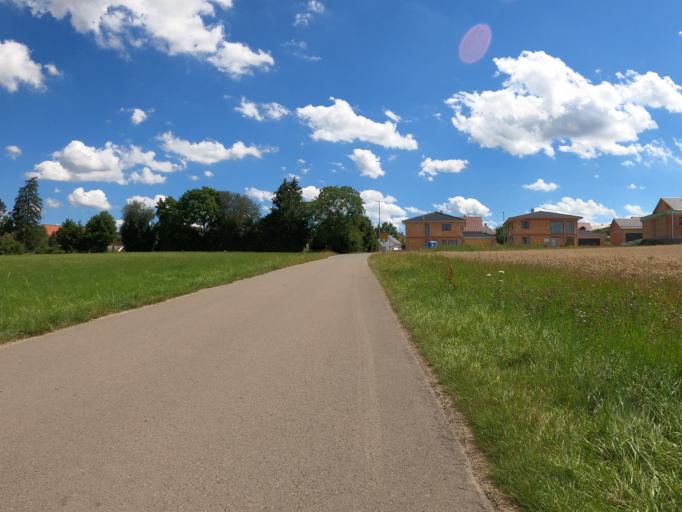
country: DE
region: Bavaria
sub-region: Swabia
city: Leipheim
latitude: 48.4023
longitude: 10.1930
